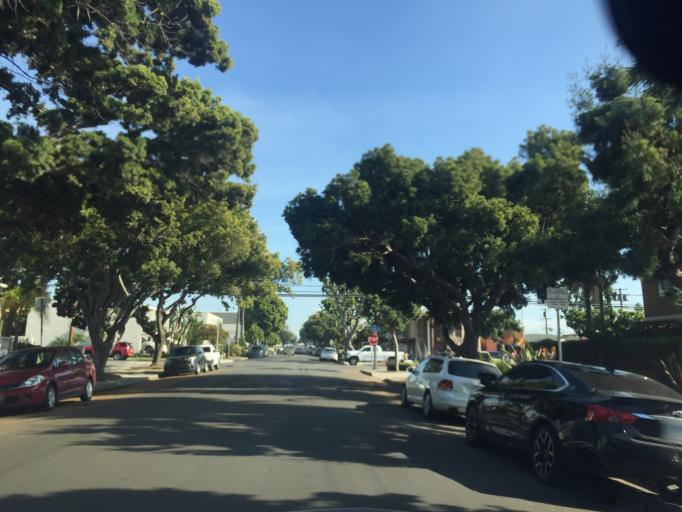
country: US
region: California
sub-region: San Diego County
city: La Jolla
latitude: 32.7994
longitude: -117.2473
